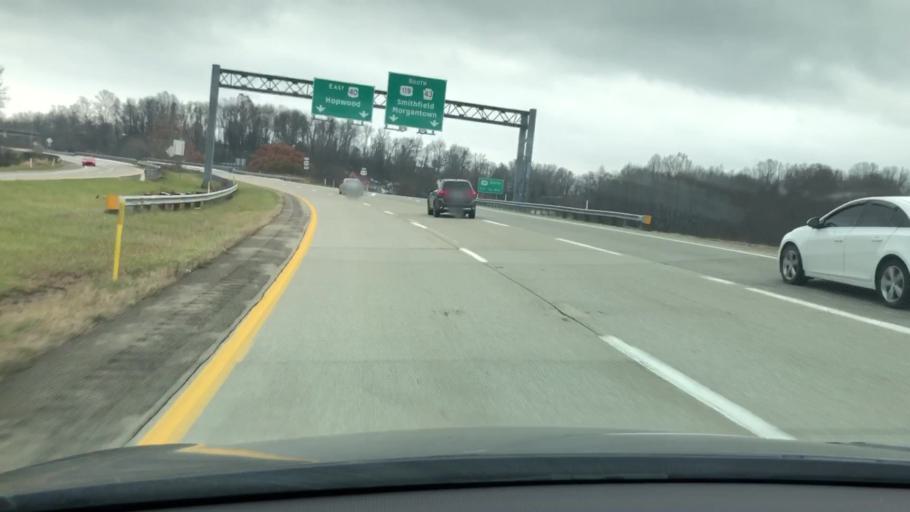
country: US
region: Pennsylvania
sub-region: Fayette County
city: Leith-Hatfield
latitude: 39.8734
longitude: -79.7454
